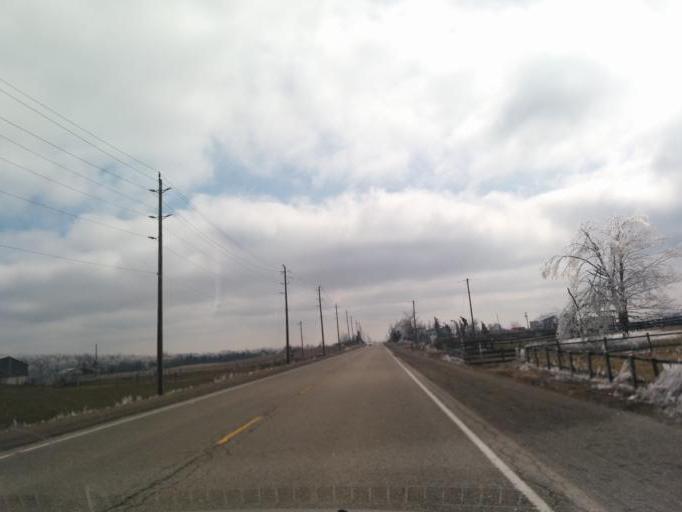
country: CA
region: Ontario
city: Waterloo
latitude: 43.6463
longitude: -80.5475
